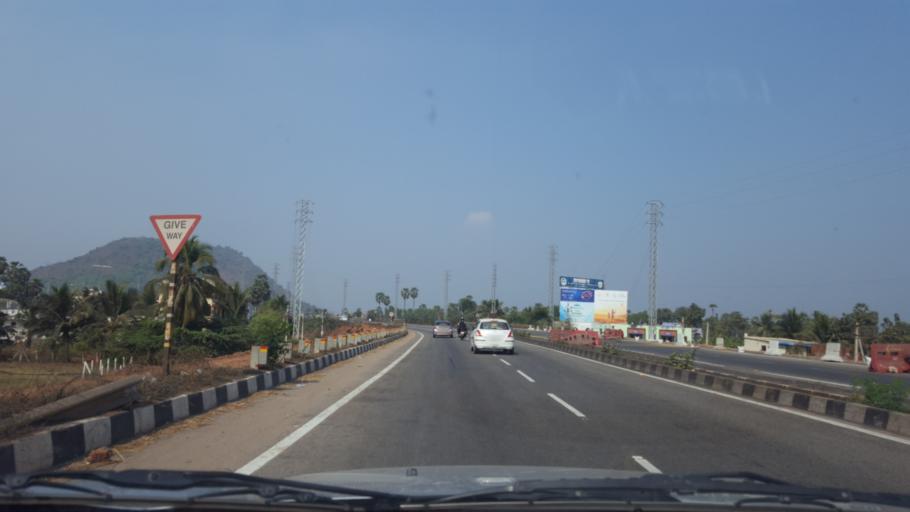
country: IN
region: Andhra Pradesh
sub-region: Vishakhapatnam
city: Bhimunipatnam
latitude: 17.8987
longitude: 83.3836
